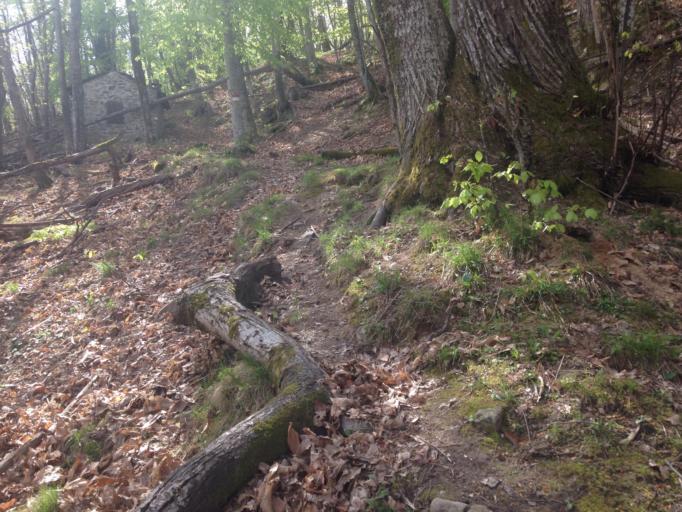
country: IT
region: Emilia-Romagna
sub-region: Provincia di Bologna
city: Lizzano in Belvedere
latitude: 44.1622
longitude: 10.8838
